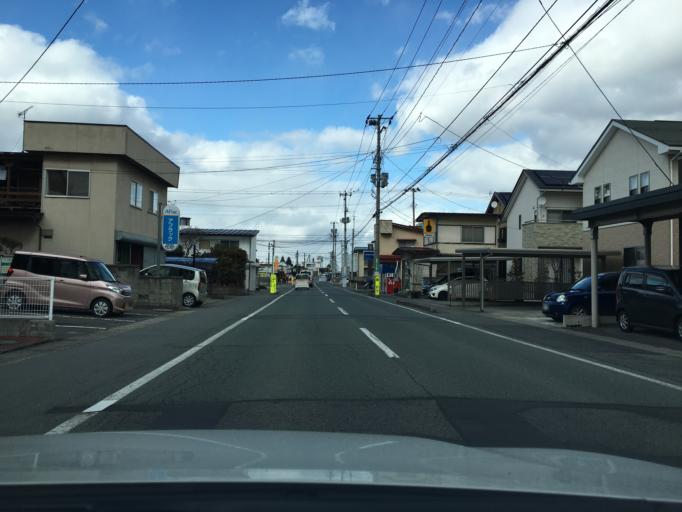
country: JP
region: Yamagata
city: Yamagata-shi
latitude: 38.2507
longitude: 140.3141
